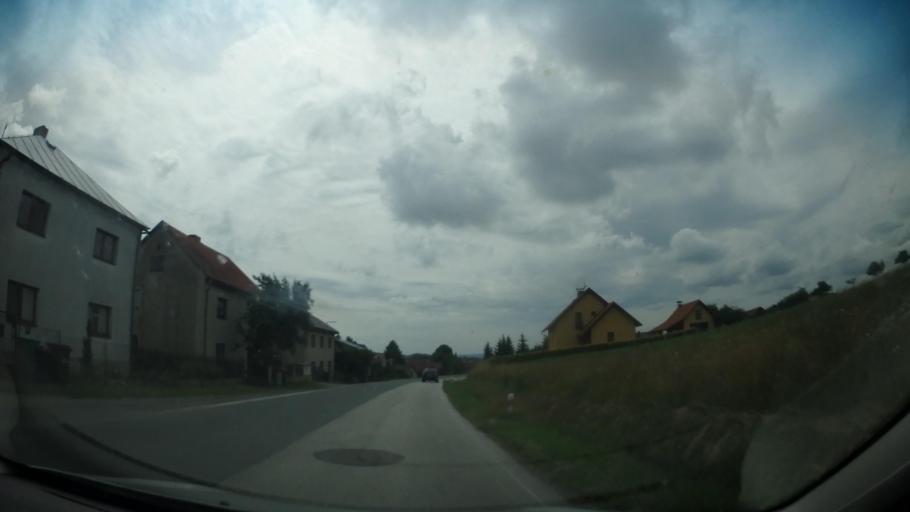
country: CZ
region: Vysocina
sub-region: Okres Zd'ar nad Sazavou
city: Nove Mesto na Morave
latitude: 49.5836
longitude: 16.0796
